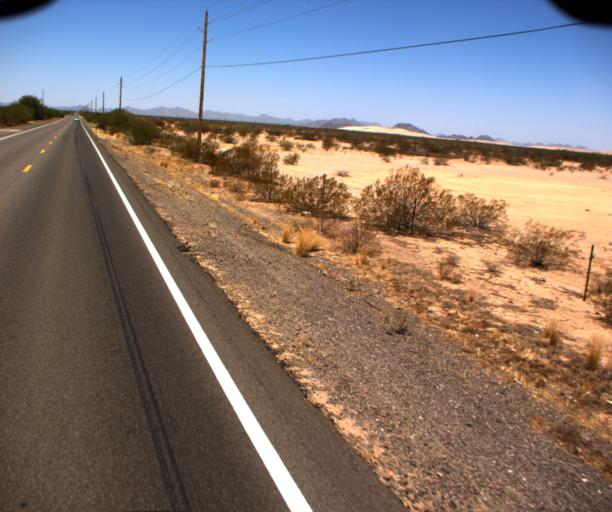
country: US
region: Arizona
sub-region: Pinal County
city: Maricopa
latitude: 33.0673
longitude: -112.2250
